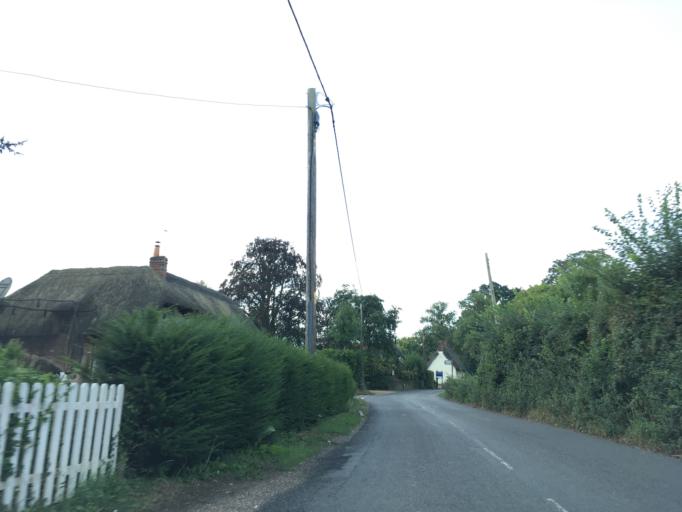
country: GB
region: England
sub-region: Hampshire
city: Andover
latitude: 51.1977
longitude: -1.3830
